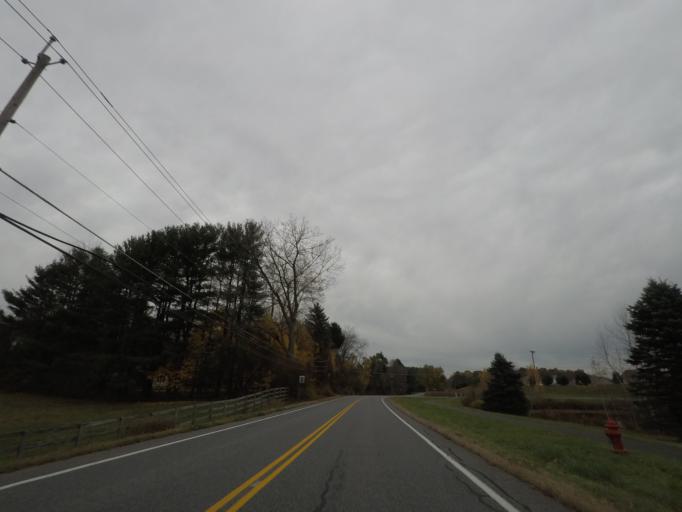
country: US
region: New York
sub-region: Schenectady County
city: Niskayuna
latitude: 42.8075
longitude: -73.8081
